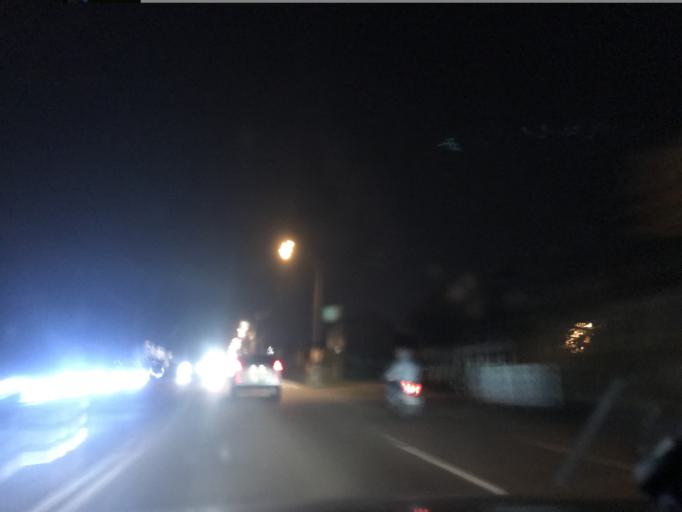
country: TW
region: Taiwan
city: Daxi
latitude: 24.8932
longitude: 121.2237
